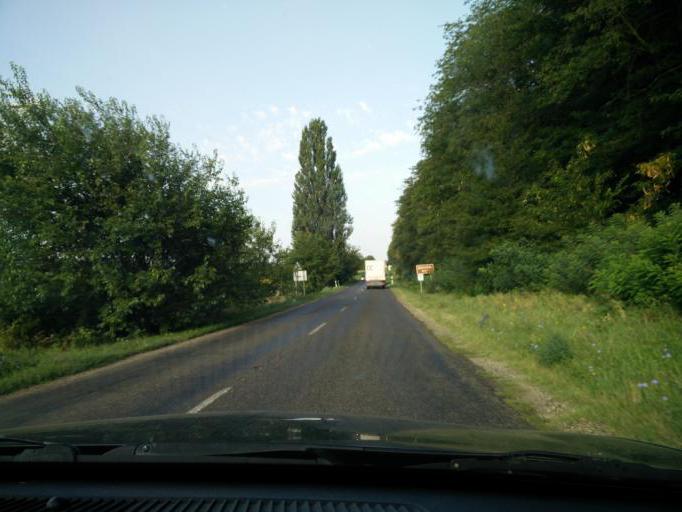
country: HU
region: Tolna
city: Nagymanyok
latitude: 46.2803
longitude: 18.4200
